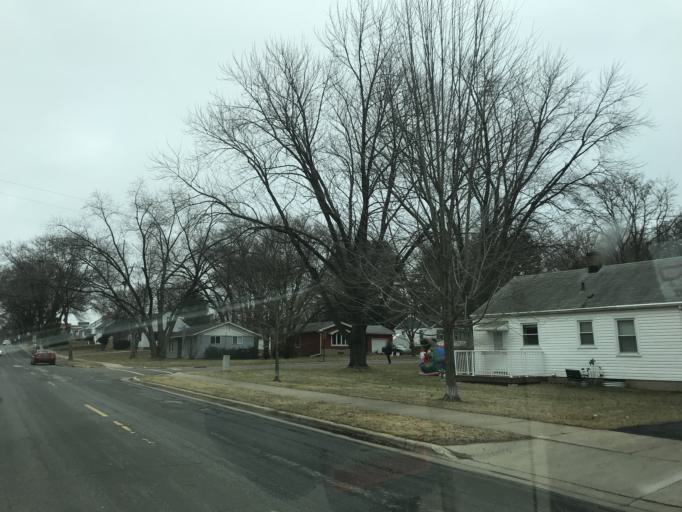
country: US
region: Wisconsin
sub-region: Dane County
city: Monona
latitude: 43.0623
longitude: -89.3316
